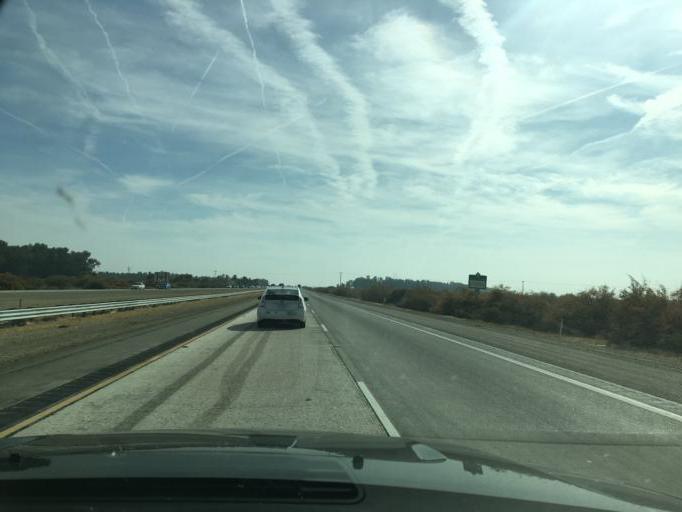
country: US
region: California
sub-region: Kern County
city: Lost Hills
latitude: 35.6046
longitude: -119.6445
